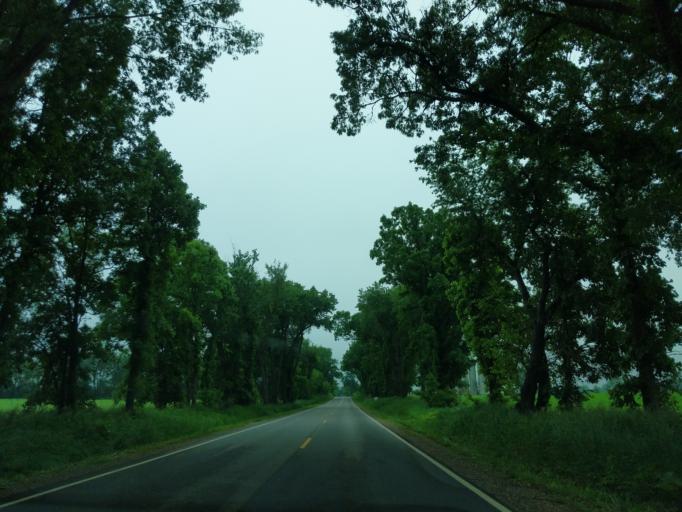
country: US
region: Michigan
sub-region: Jackson County
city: Spring Arbor
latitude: 42.2096
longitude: -84.5702
